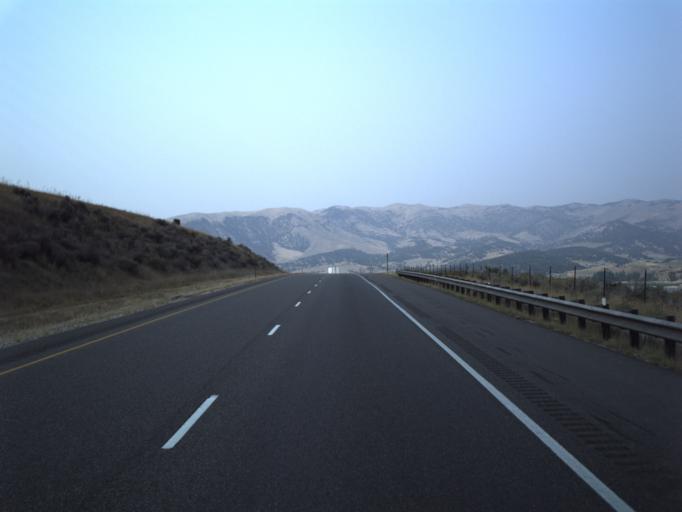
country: US
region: Utah
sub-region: Summit County
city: Coalville
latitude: 40.9321
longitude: -111.4092
